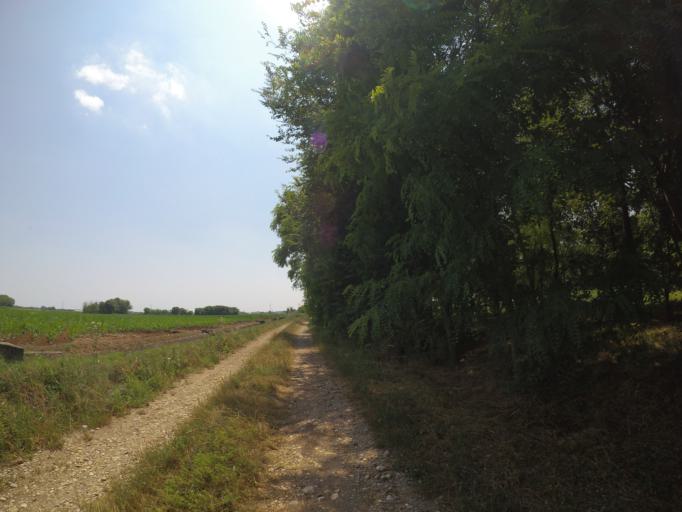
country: IT
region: Friuli Venezia Giulia
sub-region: Provincia di Udine
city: Bertiolo
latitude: 45.9589
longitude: 13.0622
